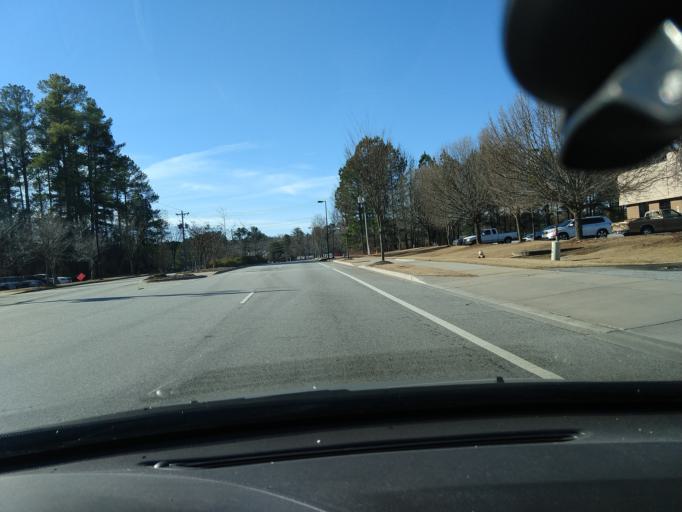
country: US
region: South Carolina
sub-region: Greenville County
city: Mauldin
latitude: 34.8016
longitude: -82.3449
